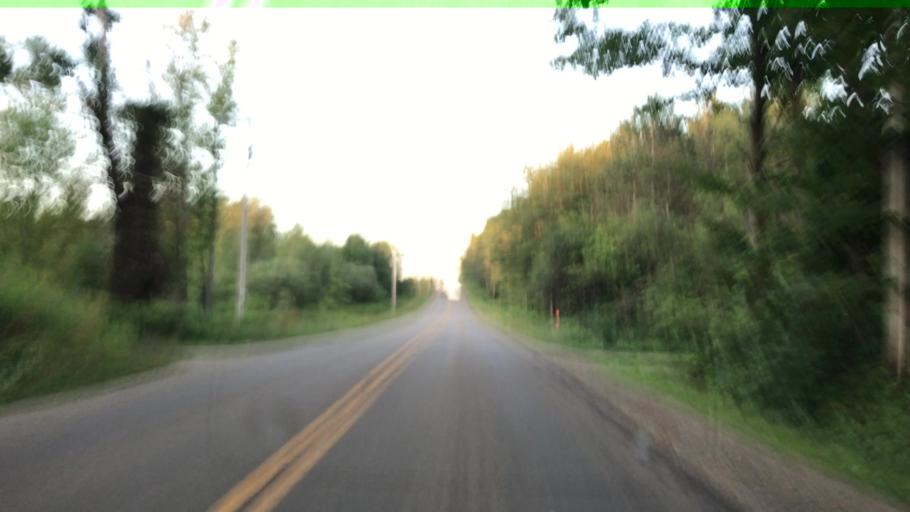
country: US
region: New York
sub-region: Chautauqua County
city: Brocton
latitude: 42.2935
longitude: -79.4128
